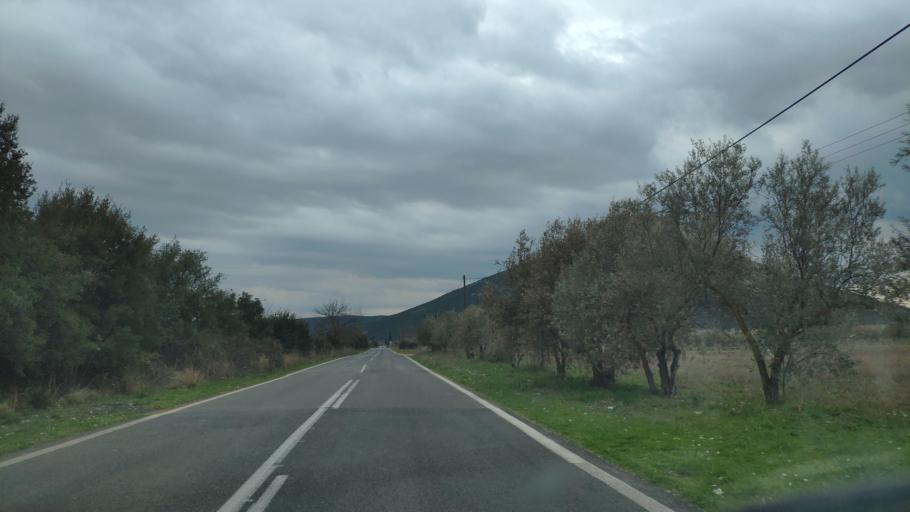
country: GR
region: Central Greece
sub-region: Nomos Fthiotidos
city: Kato Tithorea
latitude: 38.5924
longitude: 22.7314
